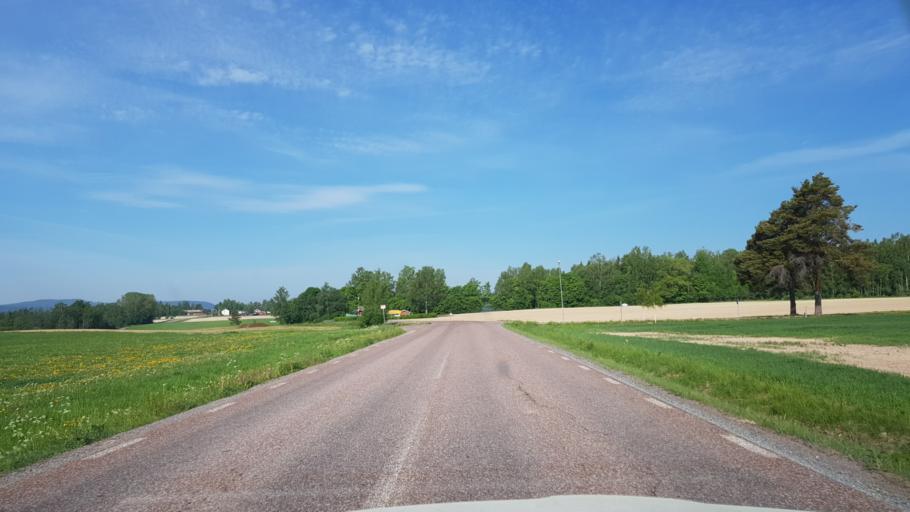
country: SE
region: Dalarna
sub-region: Borlange Kommun
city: Ornas
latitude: 60.4259
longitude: 15.6386
